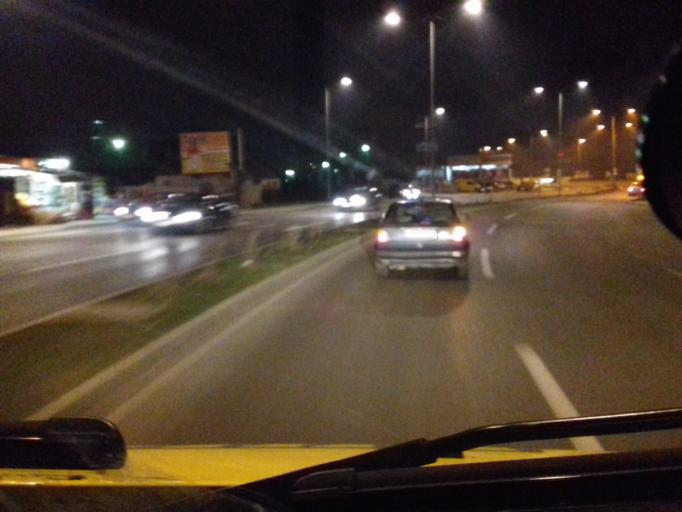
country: BA
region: Federation of Bosnia and Herzegovina
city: Zenica
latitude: 44.2032
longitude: 17.9030
